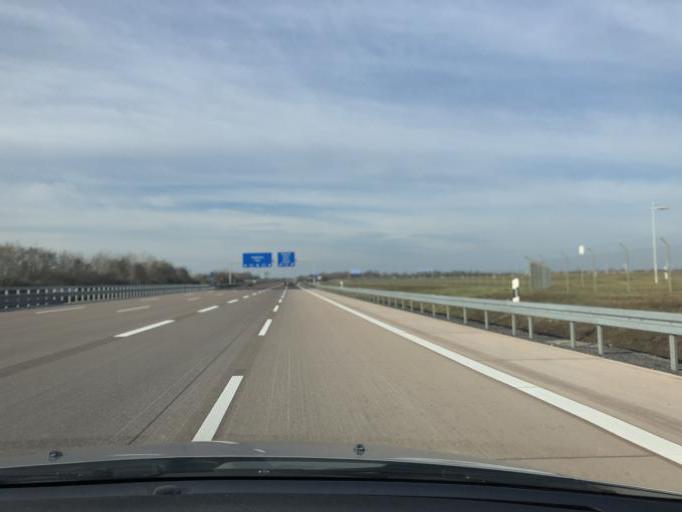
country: DE
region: Saxony
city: Schkeuditz
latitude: 51.4271
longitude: 12.2097
